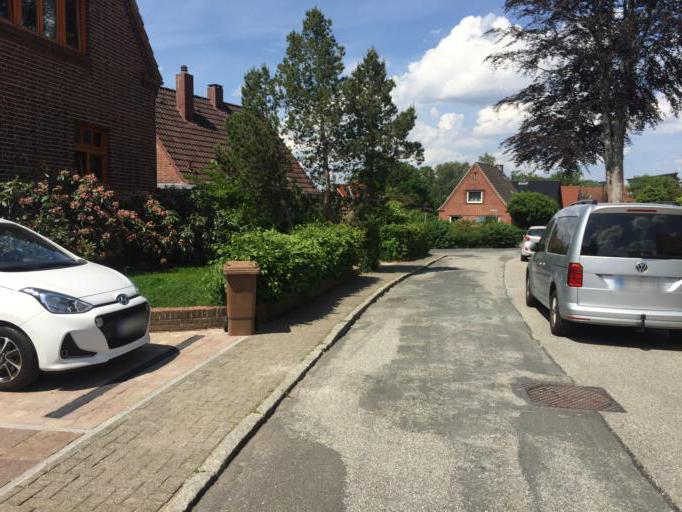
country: DE
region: Schleswig-Holstein
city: Itzehoe
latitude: 53.9291
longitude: 9.5252
